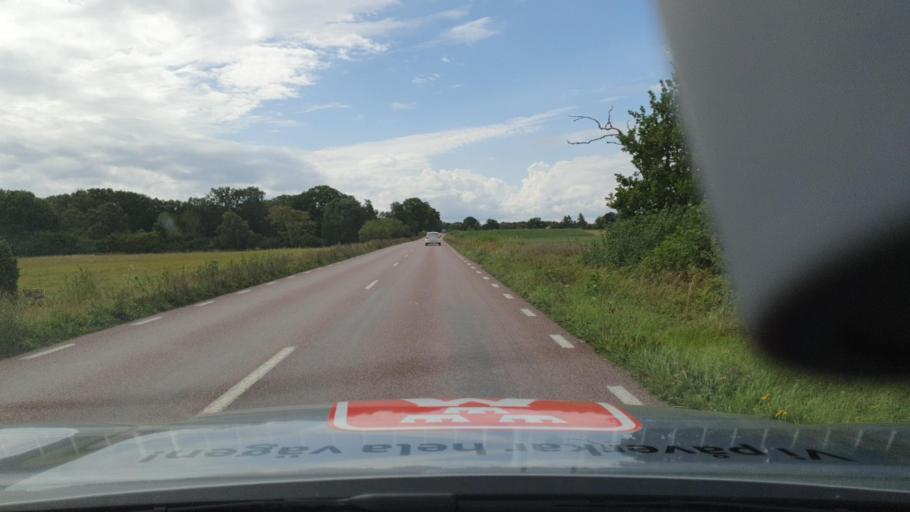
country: SE
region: Gotland
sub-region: Gotland
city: Hemse
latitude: 57.0679
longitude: 18.2996
